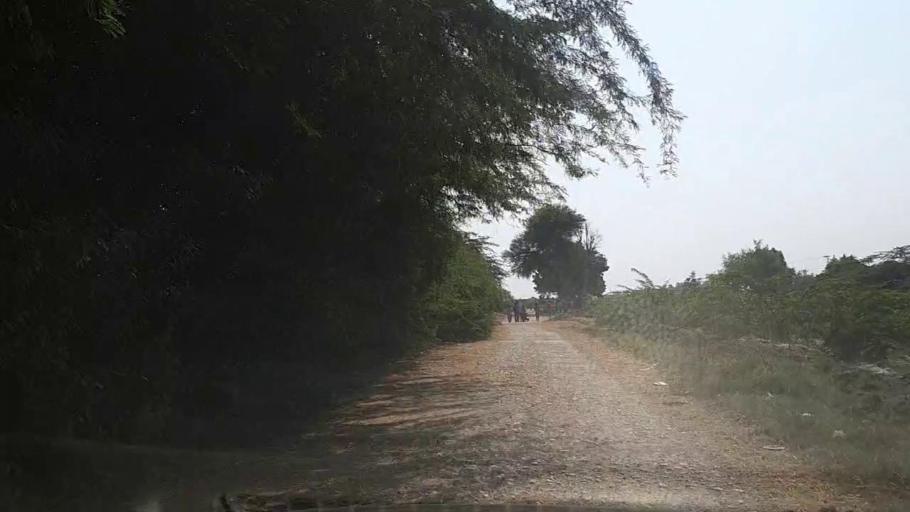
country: PK
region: Sindh
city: Thatta
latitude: 24.7837
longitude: 67.8291
